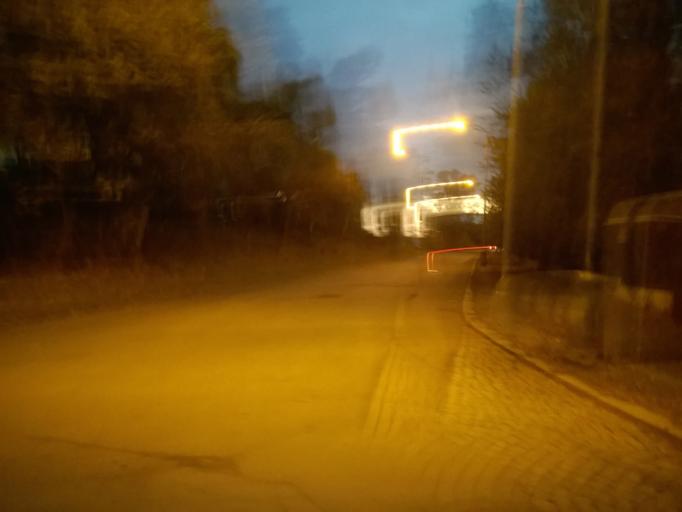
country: CZ
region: Praha
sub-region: Praha 9
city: Vysocany
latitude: 50.0983
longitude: 14.5057
